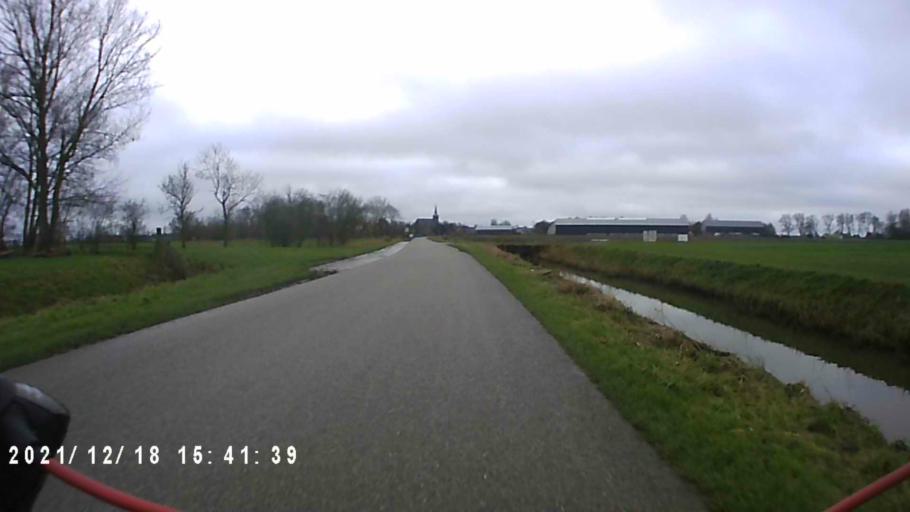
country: NL
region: Friesland
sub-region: Gemeente Dongeradeel
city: Anjum
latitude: 53.3352
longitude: 6.1065
